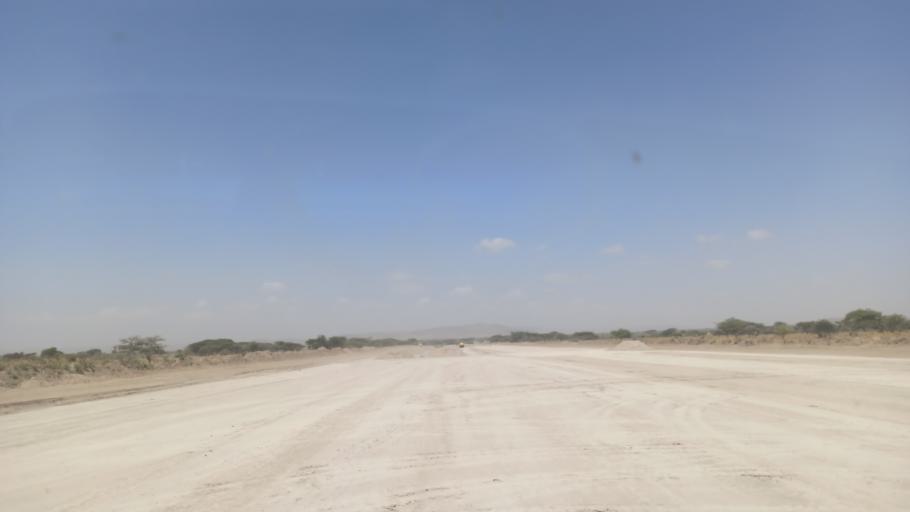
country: ET
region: Oromiya
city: Ziway
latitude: 7.7439
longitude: 38.6181
